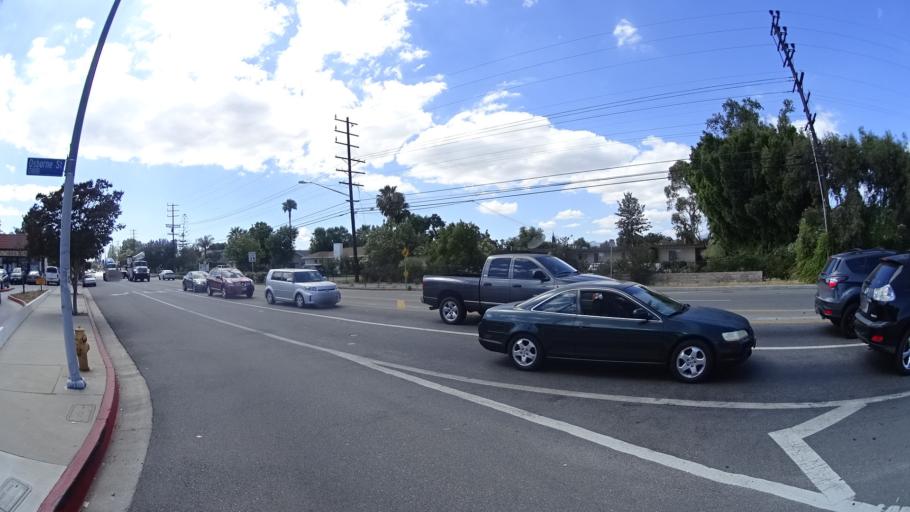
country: US
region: California
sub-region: Los Angeles County
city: San Fernando
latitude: 34.2351
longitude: -118.4359
